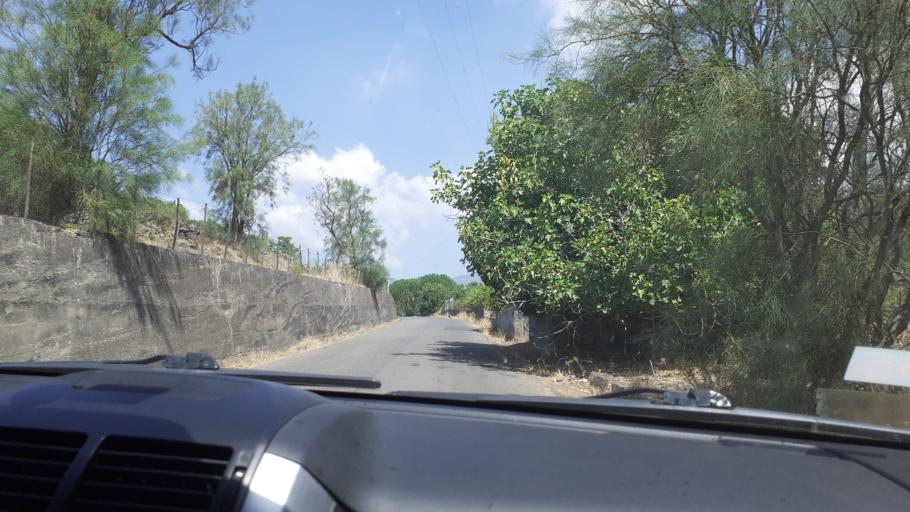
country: IT
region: Sicily
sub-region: Catania
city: Nicolosi
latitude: 37.6354
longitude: 15.0246
